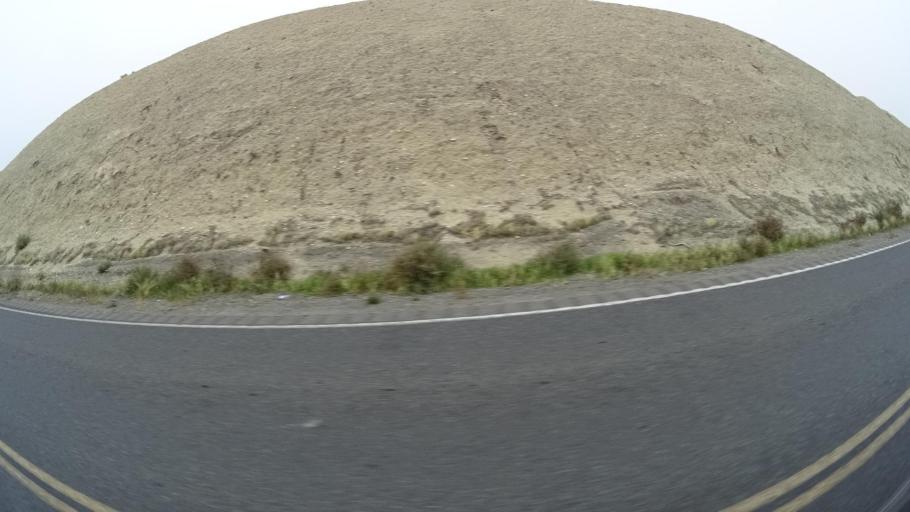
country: US
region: California
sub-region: Kern County
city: Buttonwillow
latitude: 35.3184
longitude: -119.4643
